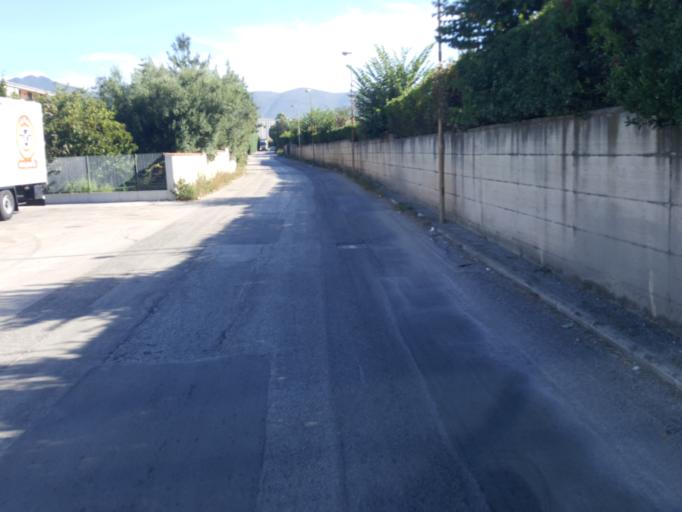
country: IT
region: Campania
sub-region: Provincia di Caserta
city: Pignataro Maggiore
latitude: 41.1617
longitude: 14.1626
